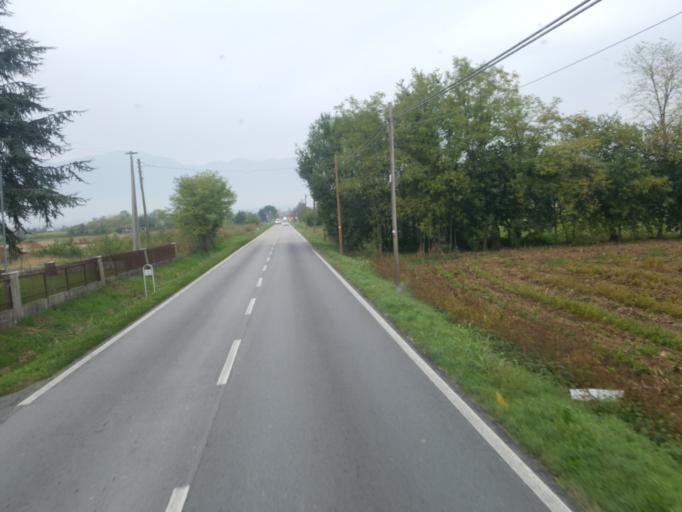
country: IT
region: Veneto
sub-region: Provincia di Treviso
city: Loria Bessica
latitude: 45.7460
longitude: 11.8659
